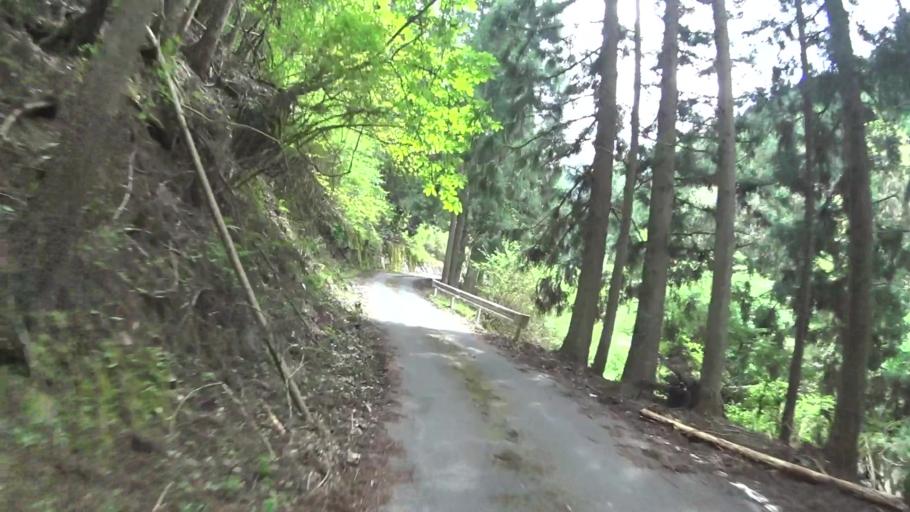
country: JP
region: Kyoto
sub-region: Kyoto-shi
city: Kamigyo-ku
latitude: 35.1842
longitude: 135.7059
